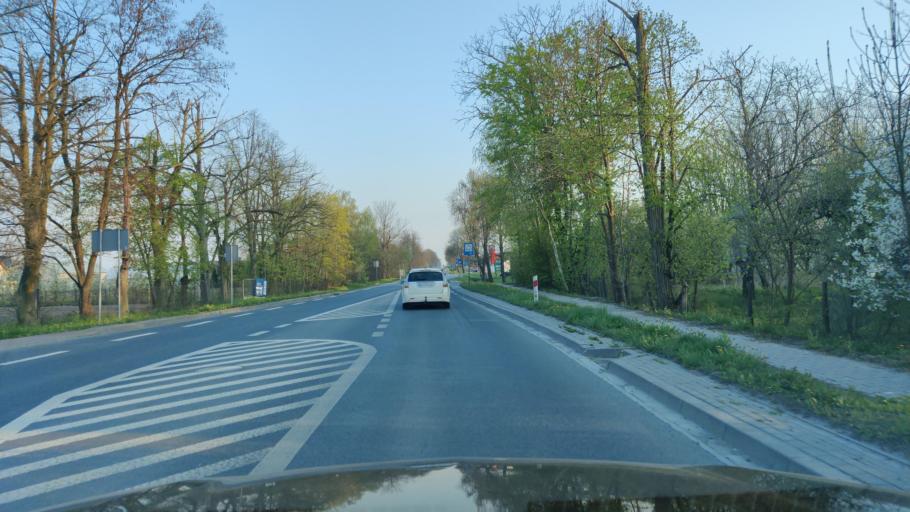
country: PL
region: Masovian Voivodeship
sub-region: Powiat pultuski
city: Pultusk
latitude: 52.6898
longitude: 21.0804
